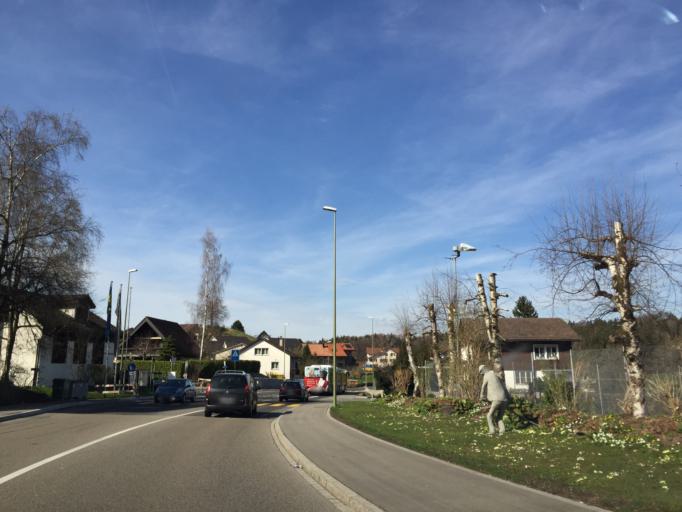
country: CH
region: Zurich
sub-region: Bezirk Horgen
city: Horgen / Allmend
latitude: 47.2155
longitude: 8.6109
